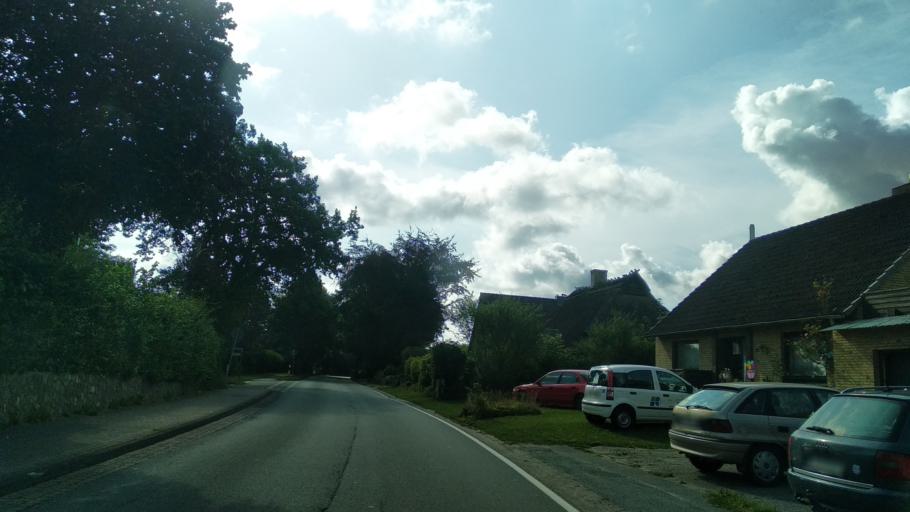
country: DE
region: Schleswig-Holstein
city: Selk
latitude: 54.4699
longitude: 9.5694
